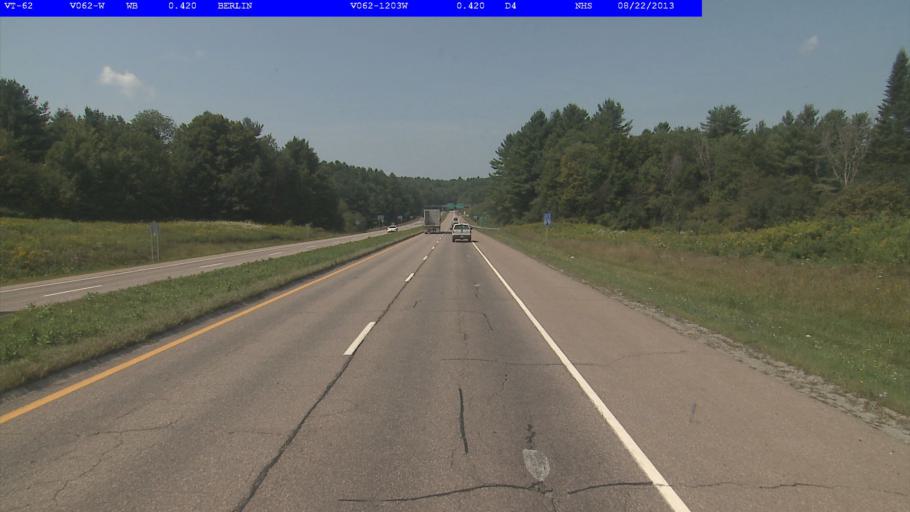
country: US
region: Vermont
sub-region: Washington County
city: Montpelier
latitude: 44.2143
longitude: -72.5763
